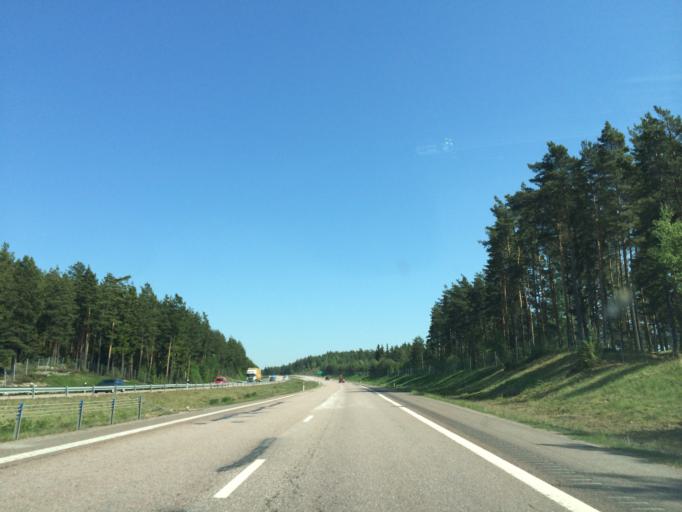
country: SE
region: Soedermanland
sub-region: Nykopings Kommun
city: Olstorp
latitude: 58.7553
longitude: 16.6347
